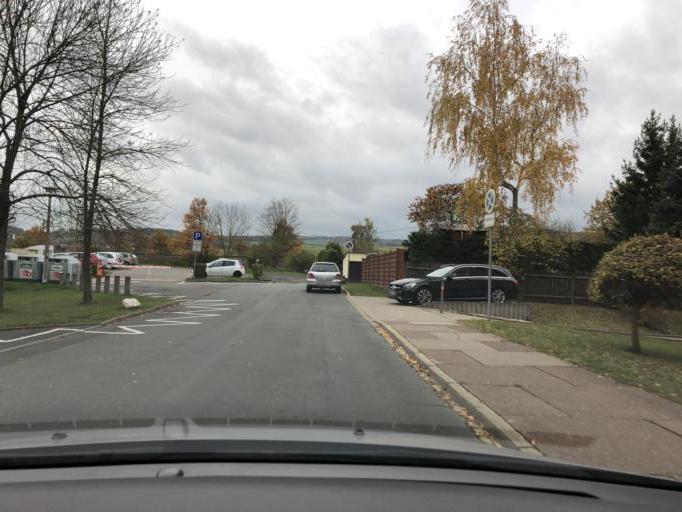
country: DE
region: Thuringia
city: Bodelwitz
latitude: 50.6957
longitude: 11.6112
